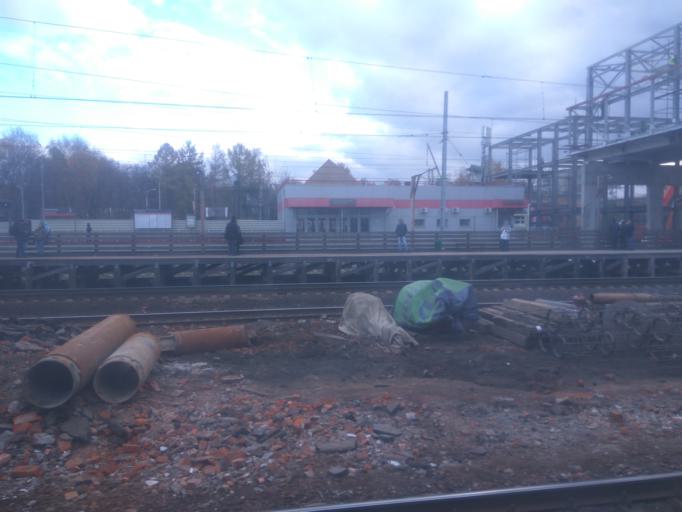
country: RU
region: Moscow
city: Solntsevo
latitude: 55.6570
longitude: 37.3845
